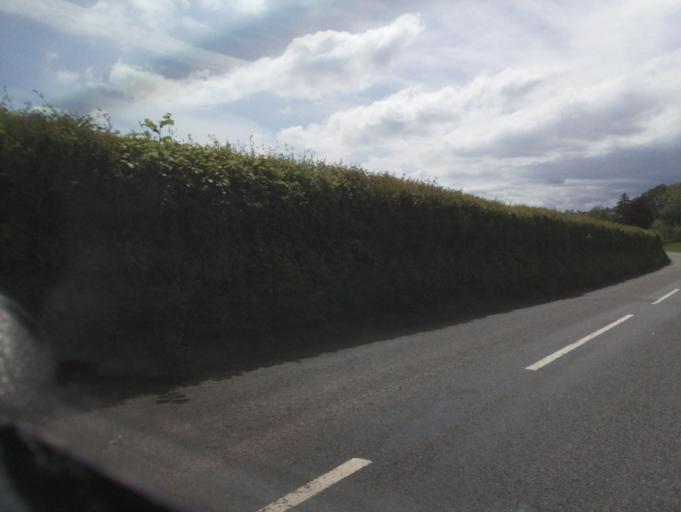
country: GB
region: England
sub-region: Herefordshire
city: Pencoyd
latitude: 51.9013
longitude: -2.7150
